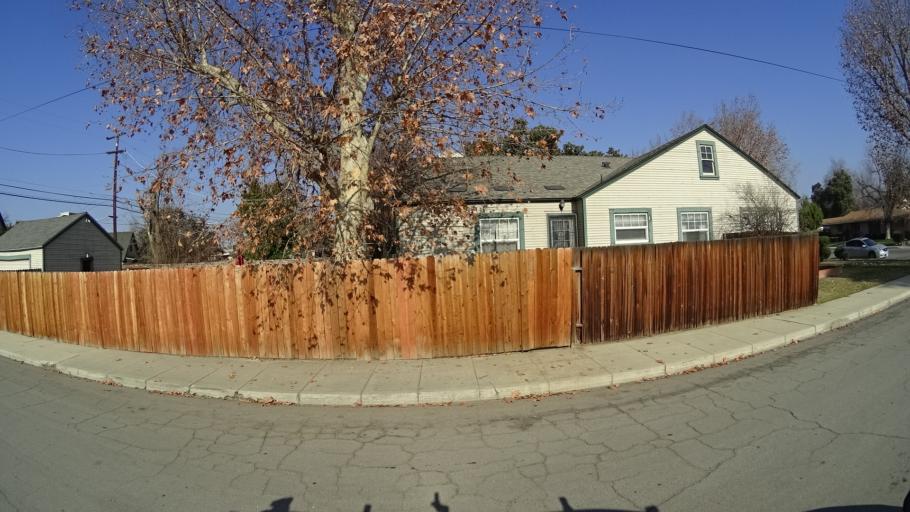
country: US
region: California
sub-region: Kern County
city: Bakersfield
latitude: 35.3892
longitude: -118.9956
